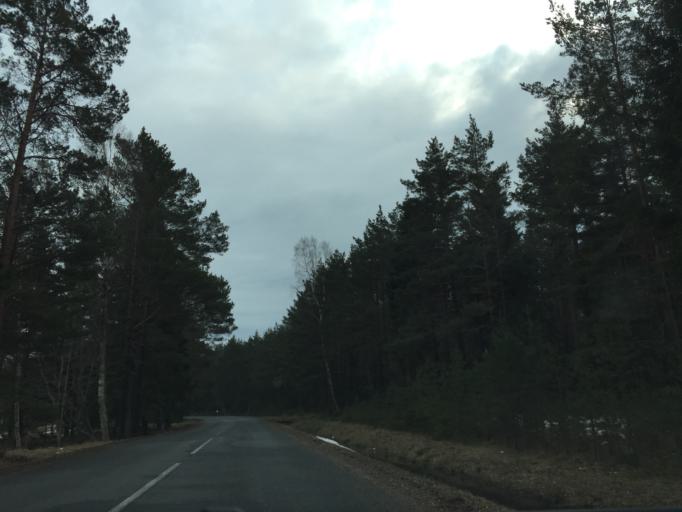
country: EE
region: Saare
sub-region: Kuressaare linn
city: Kuressaare
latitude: 58.4428
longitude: 22.0572
